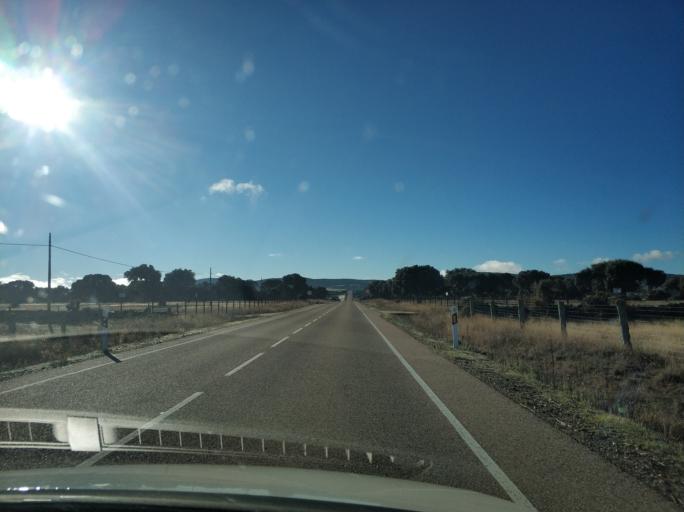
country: ES
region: Castille and Leon
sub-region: Provincia de Salamanca
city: Vecinos
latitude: 40.7556
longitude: -5.8828
